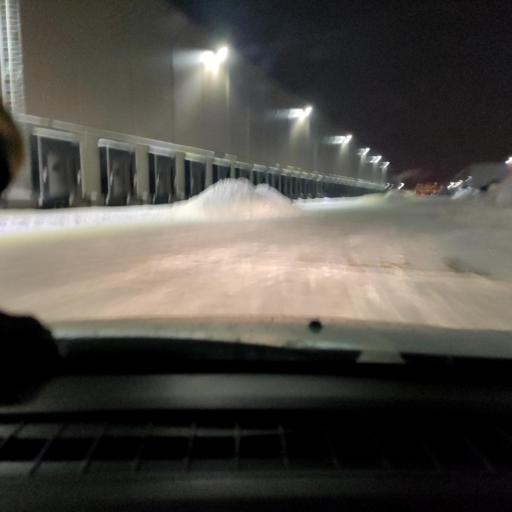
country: RU
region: Samara
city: Samara
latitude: 53.0956
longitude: 50.1256
